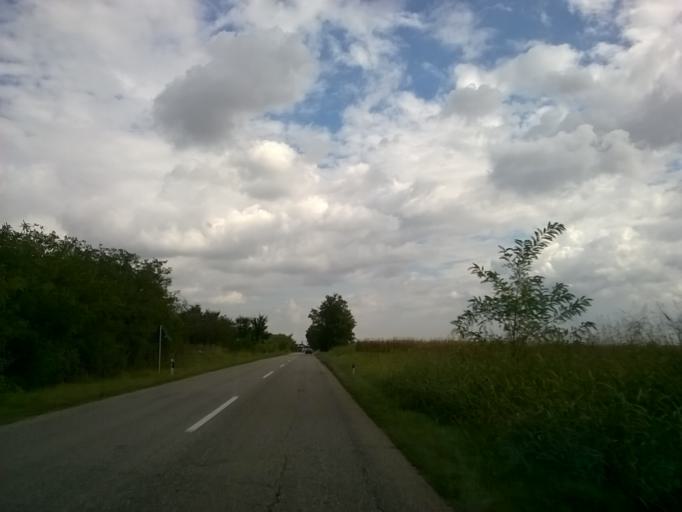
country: RS
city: Padina
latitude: 45.1183
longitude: 20.7001
